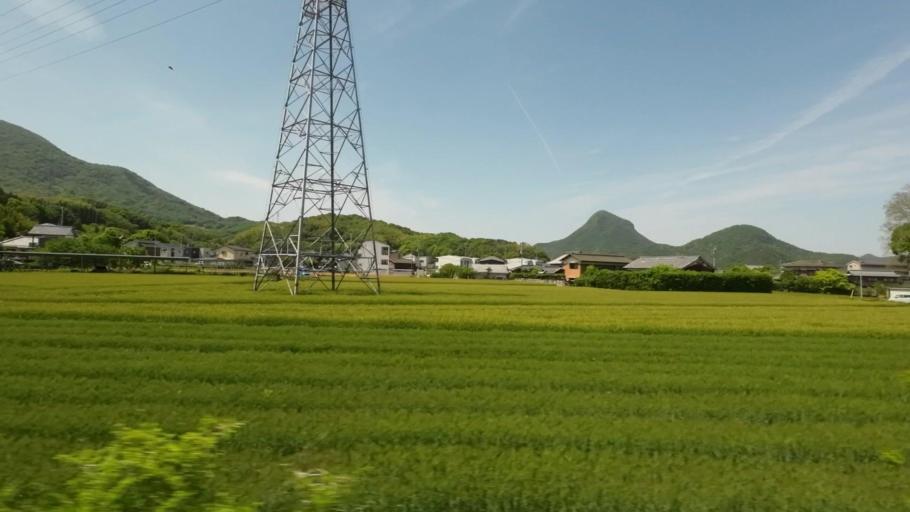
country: JP
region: Kagawa
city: Marugame
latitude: 34.2245
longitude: 133.7925
